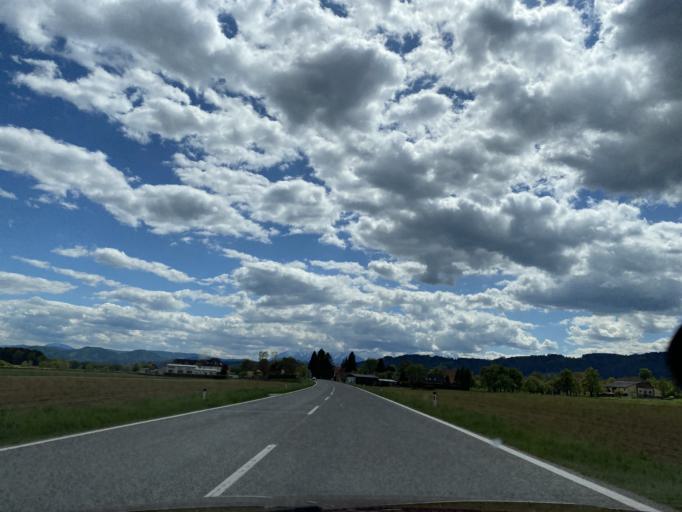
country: AT
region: Carinthia
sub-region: Politischer Bezirk Wolfsberg
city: Sankt Andrae
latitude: 46.7938
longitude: 14.8261
